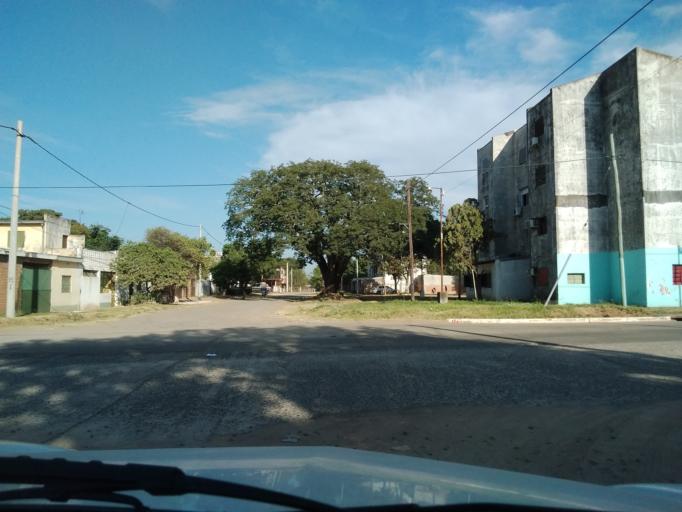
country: AR
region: Corrientes
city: Corrientes
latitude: -27.4938
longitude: -58.7853
